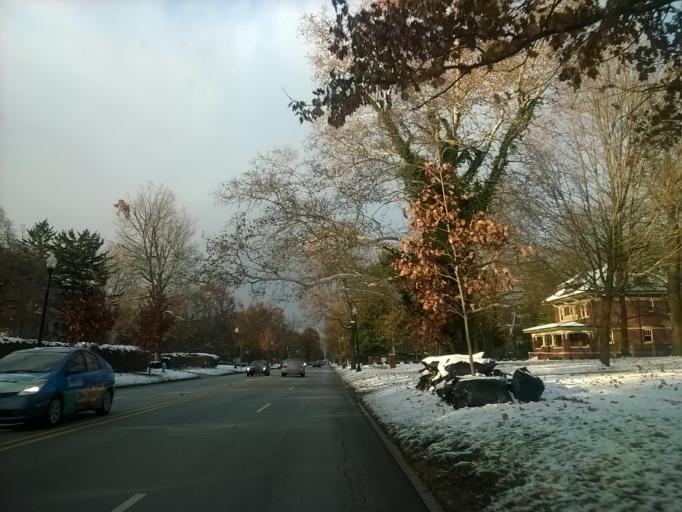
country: US
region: Indiana
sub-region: Marion County
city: Broad Ripple
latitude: 39.8294
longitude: -86.1568
